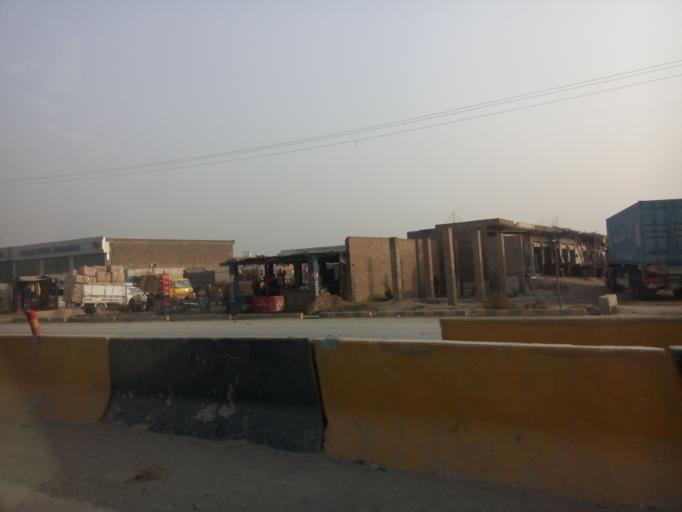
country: PK
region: Khyber Pakhtunkhwa
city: Peshawar
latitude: 33.9846
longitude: 71.5743
